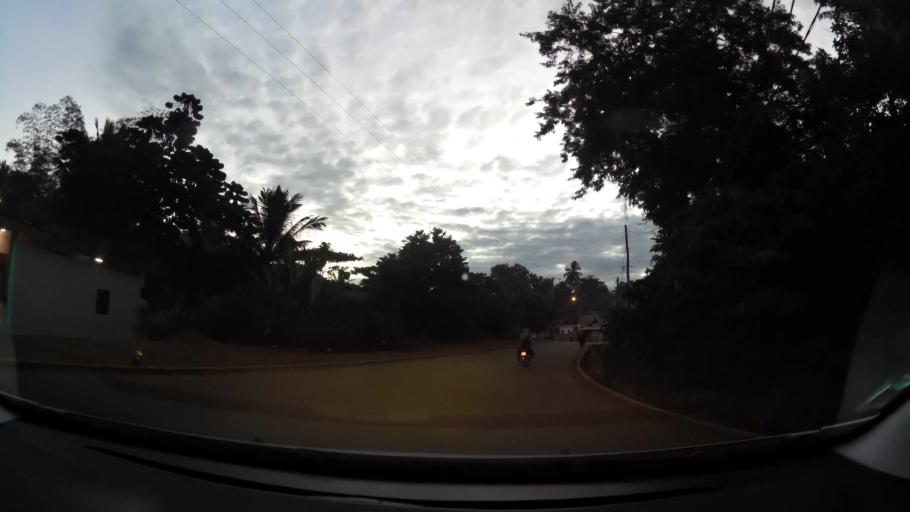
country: YT
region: Bandraboua
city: Bandraboua
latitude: -12.7214
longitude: 45.1166
